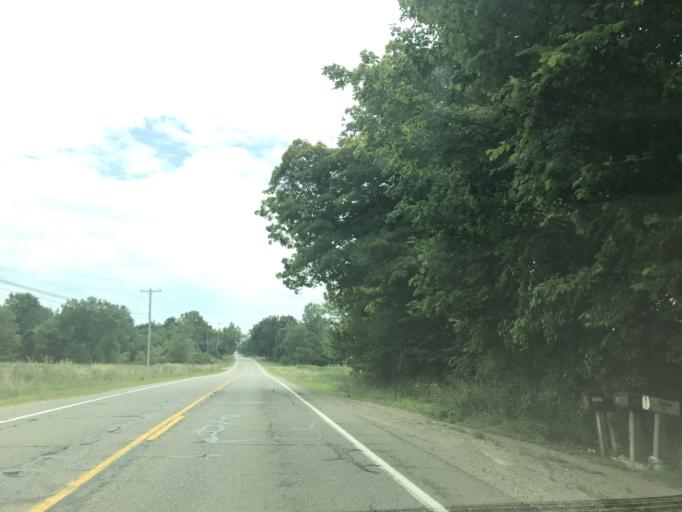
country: US
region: Michigan
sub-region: Clinton County
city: Wacousta
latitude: 42.7944
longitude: -84.7215
